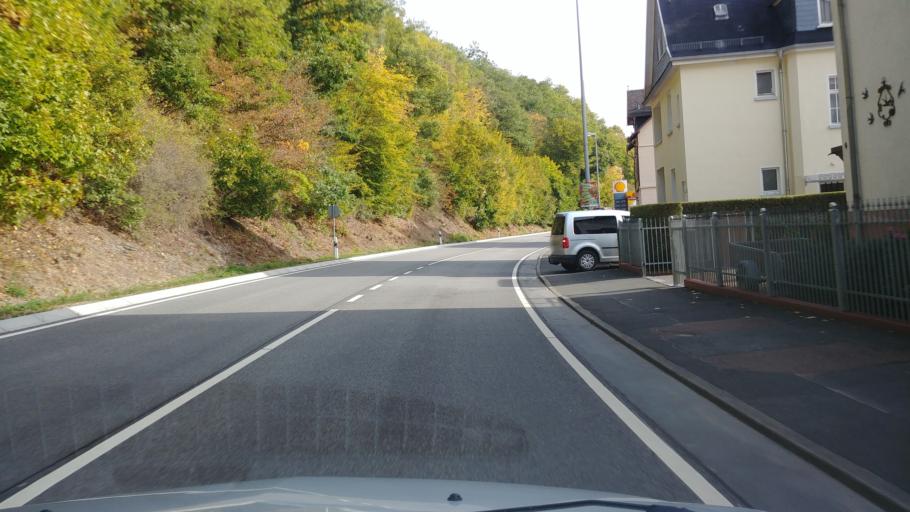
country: DE
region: Rheinland-Pfalz
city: Eisighofen
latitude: 50.2329
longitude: 8.0549
